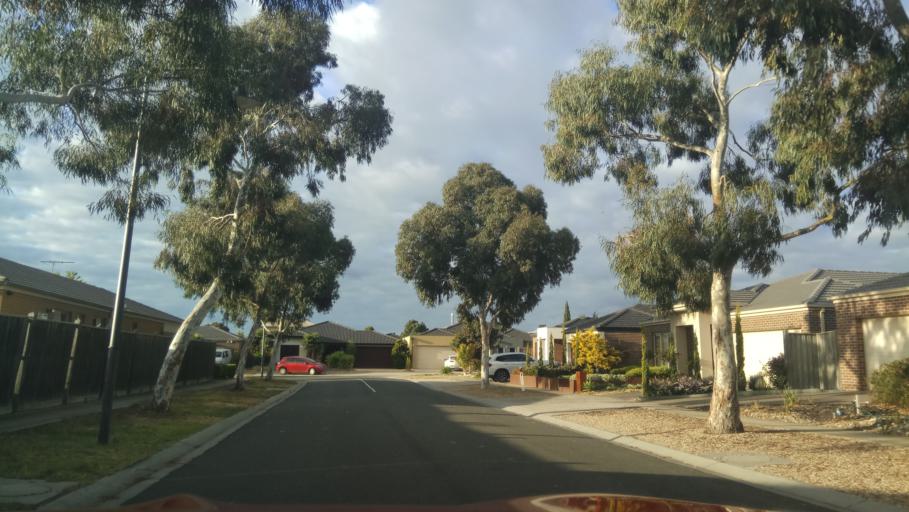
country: AU
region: Victoria
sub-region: Wyndham
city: Point Cook
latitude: -37.9033
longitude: 144.7444
